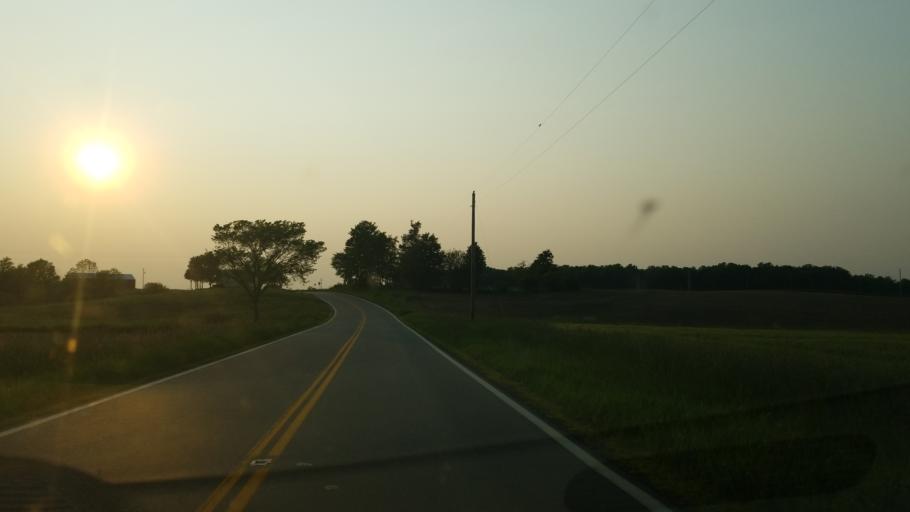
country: US
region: Ohio
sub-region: Ashland County
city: Ashland
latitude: 40.9571
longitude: -82.3382
